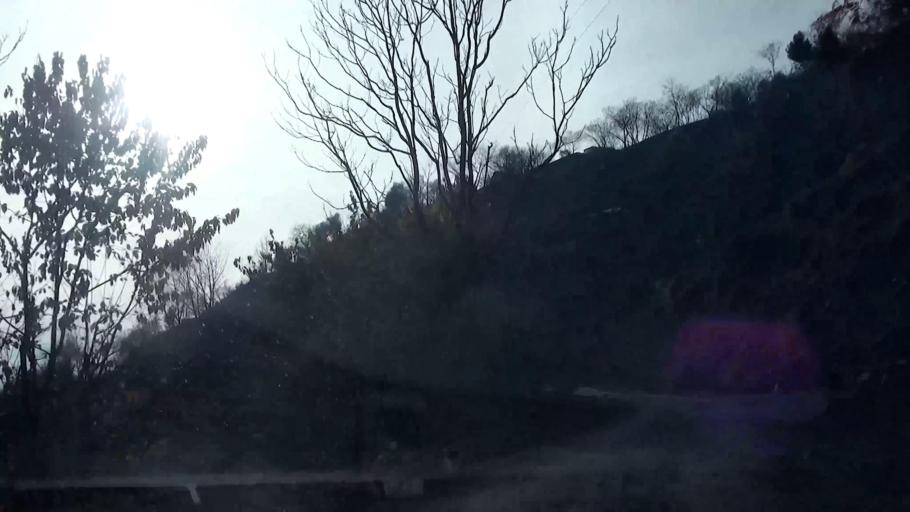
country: PK
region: Azad Kashmir
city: Muzaffarabad
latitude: 34.3666
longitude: 73.5276
